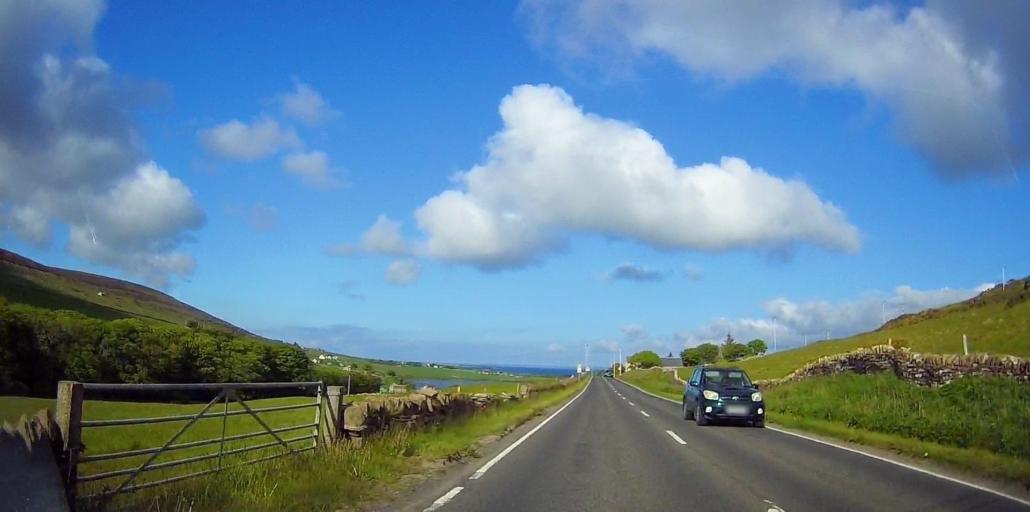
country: GB
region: Scotland
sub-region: Orkney Islands
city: Stromness
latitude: 59.0077
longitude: -3.1337
